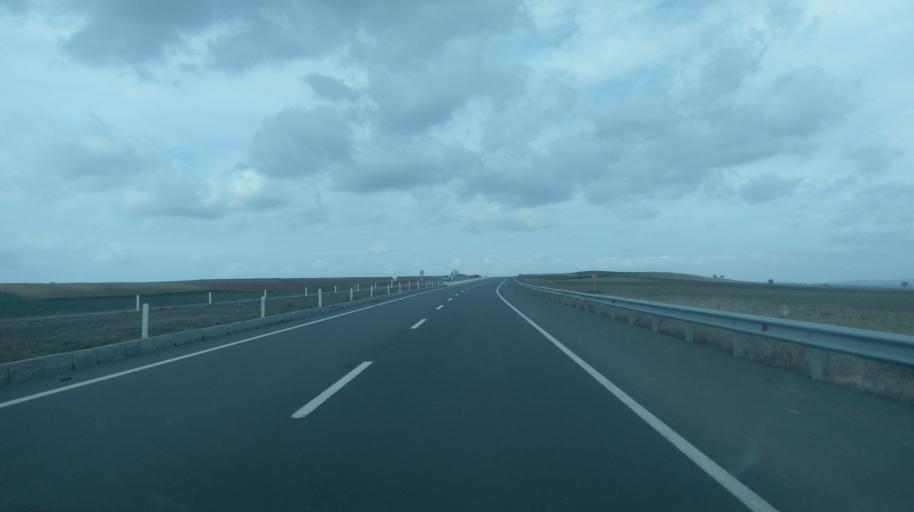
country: TR
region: Edirne
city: Ibriktepe
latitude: 41.0123
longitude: 26.6366
